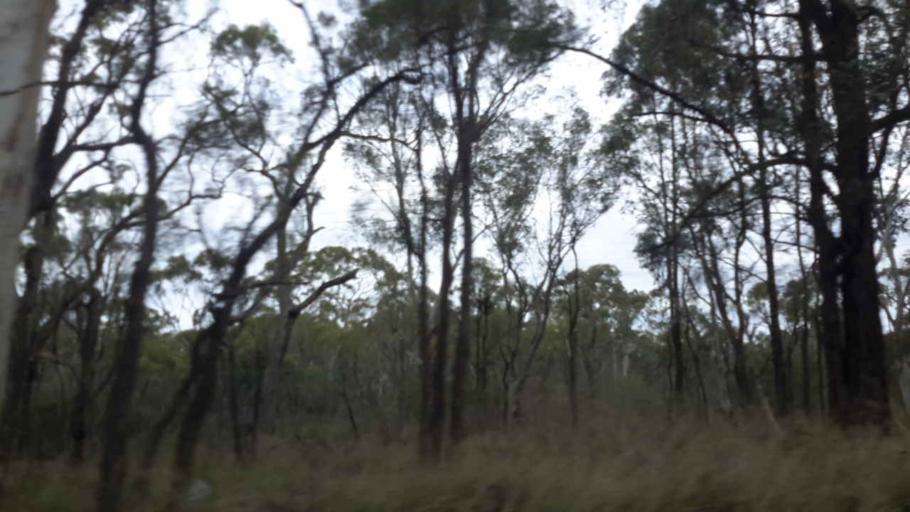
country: AU
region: New South Wales
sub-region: Hawkesbury
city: South Windsor
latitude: -33.6554
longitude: 150.7713
